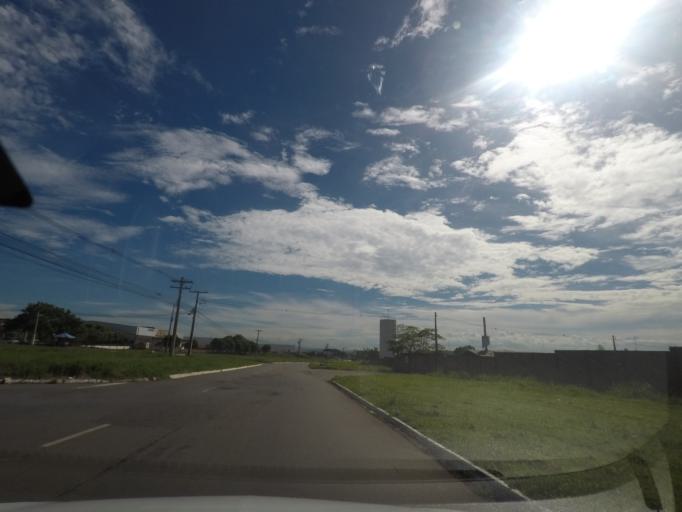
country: BR
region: Goias
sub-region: Aparecida De Goiania
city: Aparecida de Goiania
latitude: -16.8017
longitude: -49.2594
